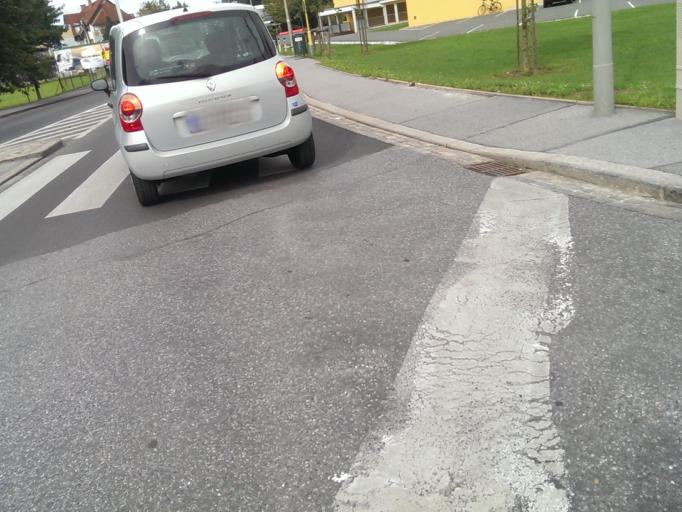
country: AT
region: Styria
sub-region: Graz Stadt
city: Graz
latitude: 47.0451
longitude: 15.4642
